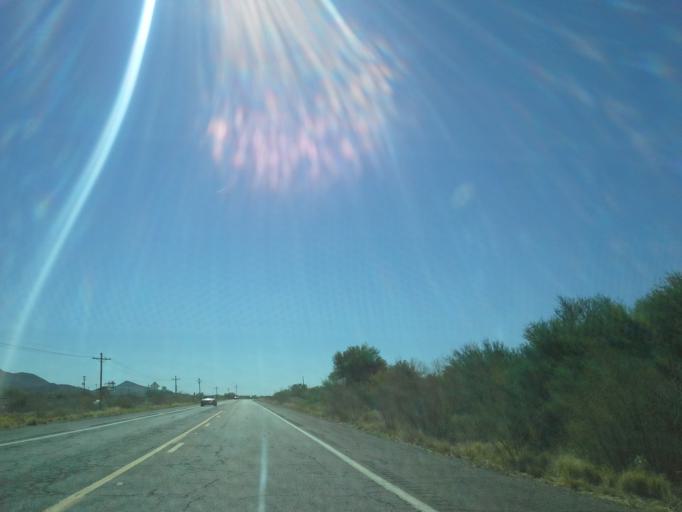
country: US
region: Arizona
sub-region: Pinal County
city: Sacaton
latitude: 33.1425
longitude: -111.7602
